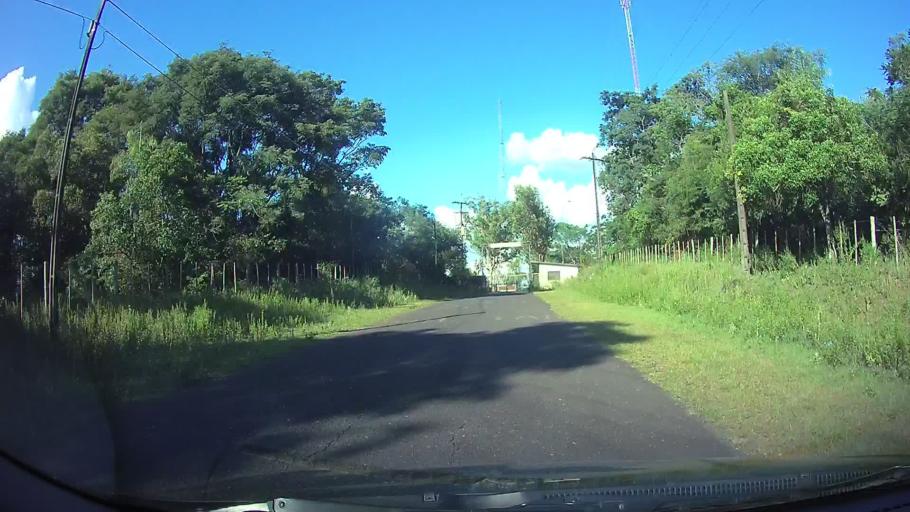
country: PY
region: Central
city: Aregua
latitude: -25.3328
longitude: -57.3784
